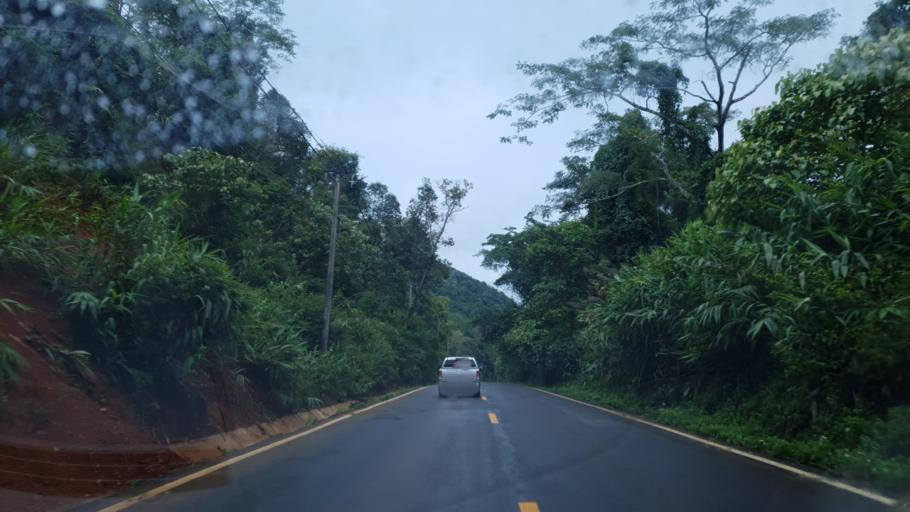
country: TH
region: Mae Hong Son
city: Ban Huai I Huak
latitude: 18.1494
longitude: 98.0970
